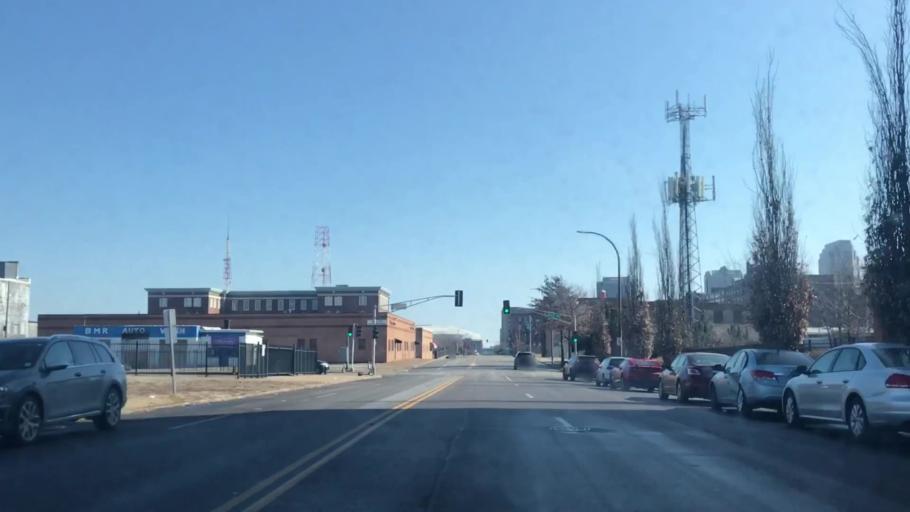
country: US
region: Missouri
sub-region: City of Saint Louis
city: St. Louis
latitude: 38.6357
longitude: -90.2080
